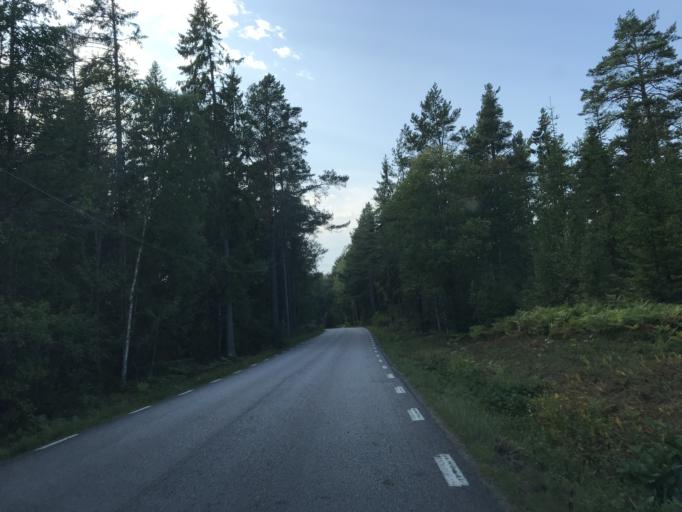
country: SE
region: Stockholm
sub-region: Norrtalje Kommun
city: Bjorko
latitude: 59.8663
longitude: 19.0298
